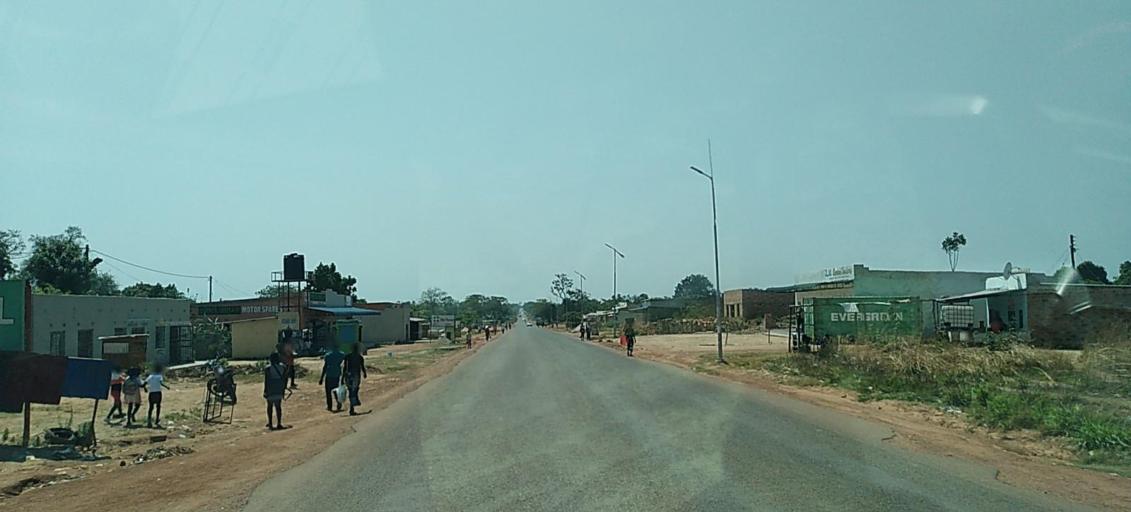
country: ZM
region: North-Western
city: Solwezi
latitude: -12.3143
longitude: 25.8531
